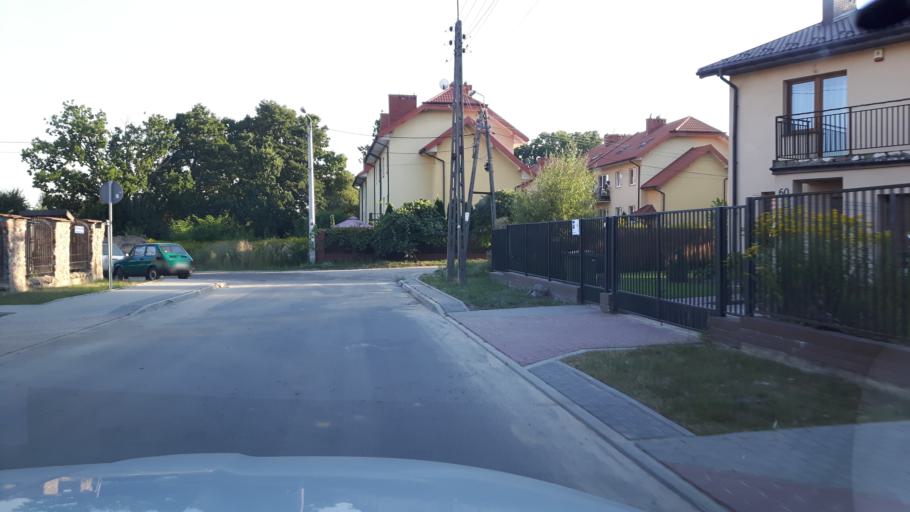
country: PL
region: Masovian Voivodeship
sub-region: Powiat wolominski
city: Kobylka
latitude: 52.3188
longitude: 21.1937
